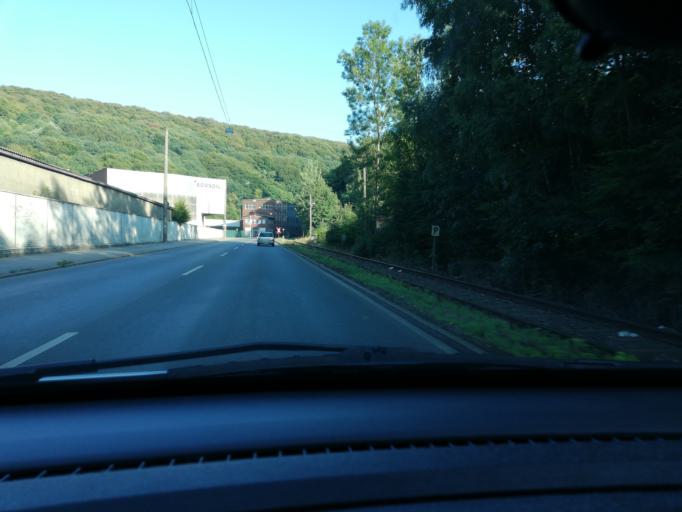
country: DE
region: North Rhine-Westphalia
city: Gevelsberg
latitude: 51.3096
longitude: 7.3435
